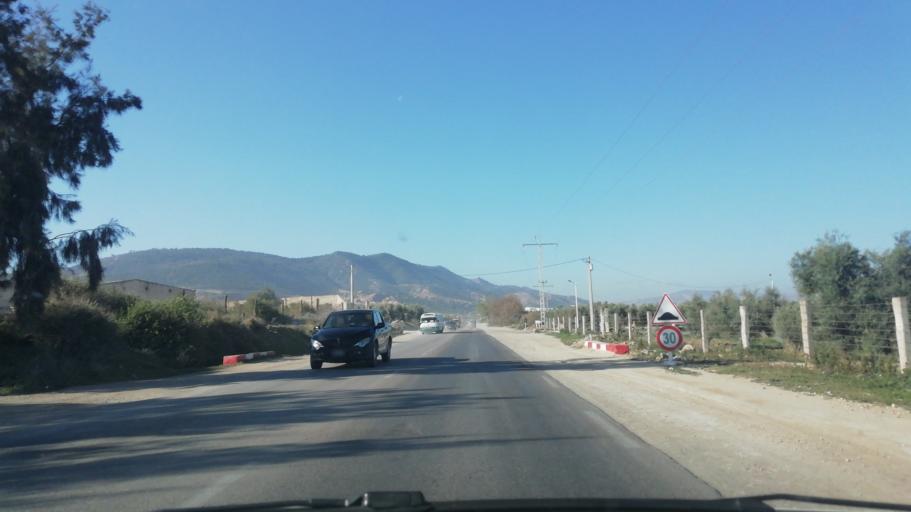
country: DZ
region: Mascara
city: Sig
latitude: 35.5352
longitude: -0.1404
